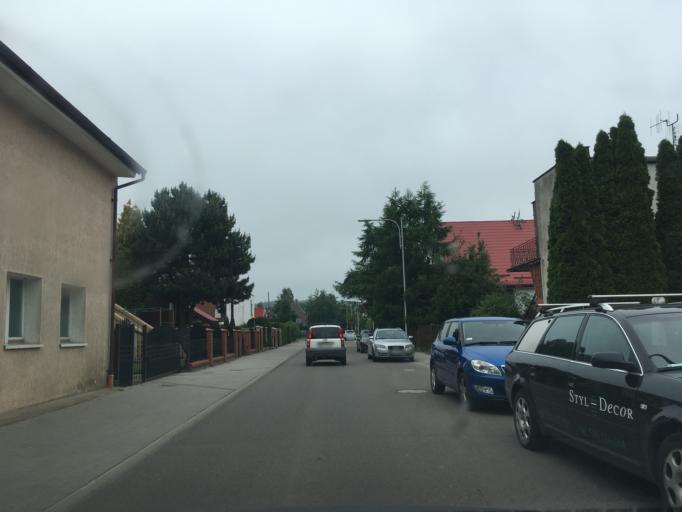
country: PL
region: West Pomeranian Voivodeship
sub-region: Koszalin
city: Koszalin
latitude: 54.1882
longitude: 16.2178
